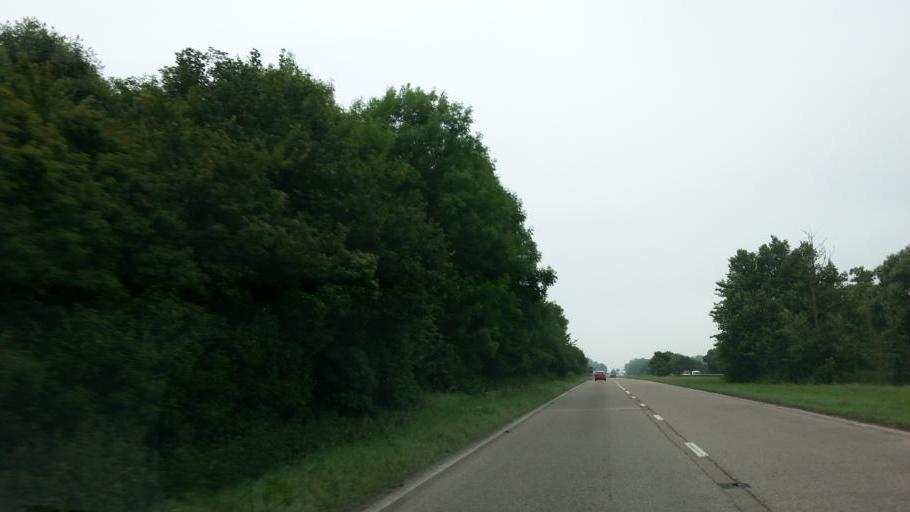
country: GB
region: England
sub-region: Leicestershire
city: Grimston
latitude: 52.7904
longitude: -1.0447
